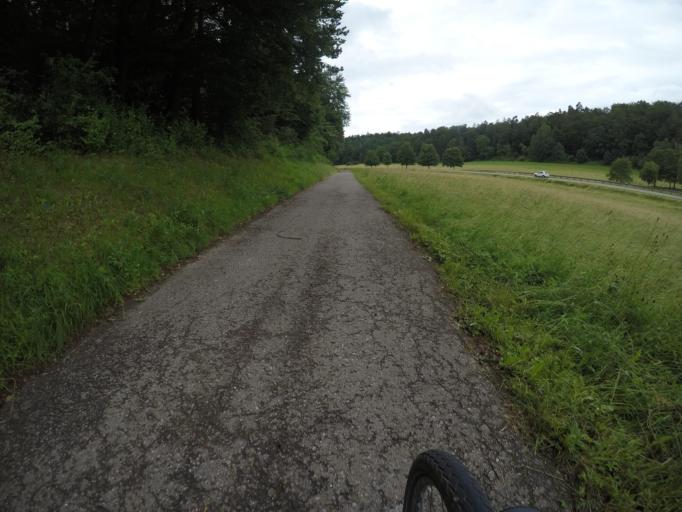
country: DE
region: Baden-Wuerttemberg
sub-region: Regierungsbezirk Stuttgart
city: Aidlingen
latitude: 48.6669
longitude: 8.8772
